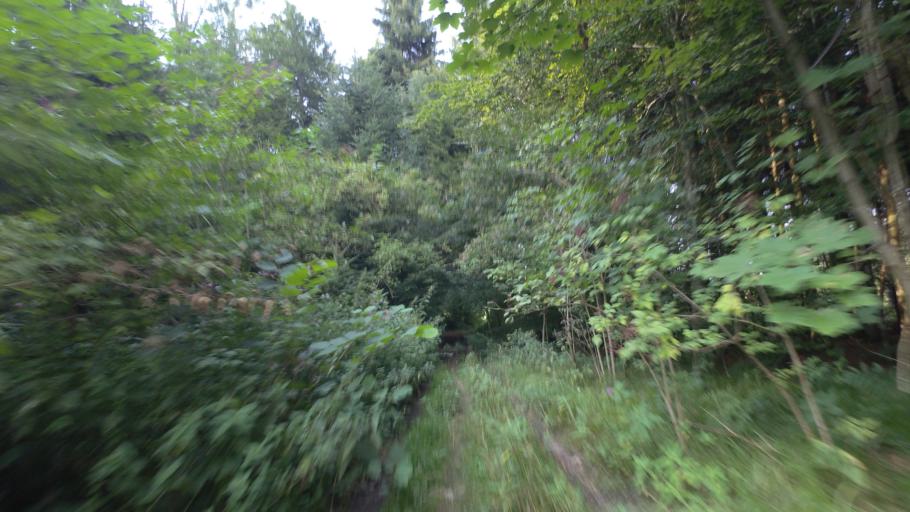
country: DE
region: Bavaria
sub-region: Upper Bavaria
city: Chieming
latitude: 47.9160
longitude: 12.5610
